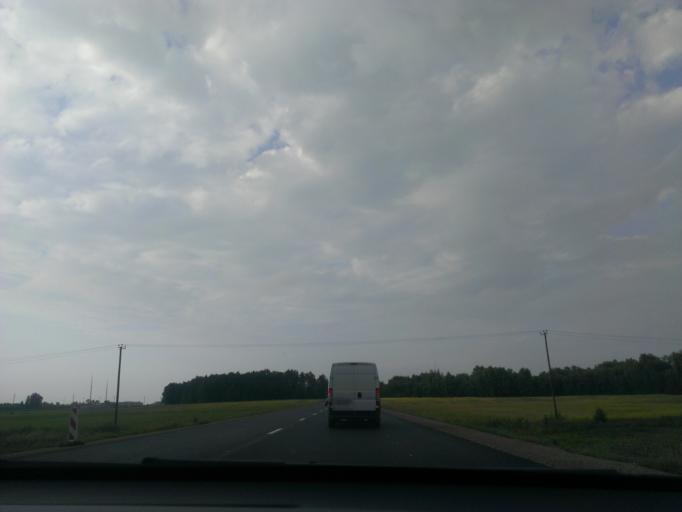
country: LV
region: Lecava
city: Iecava
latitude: 56.6483
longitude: 24.2287
